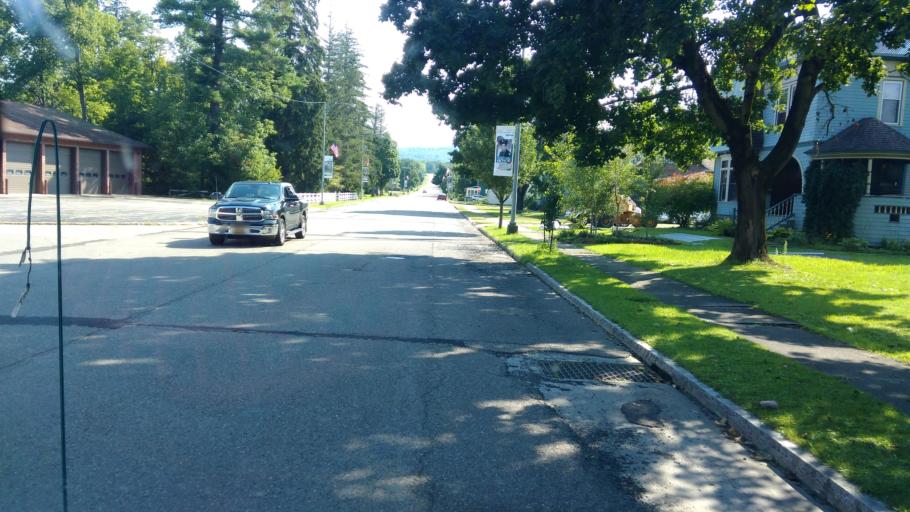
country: US
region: New York
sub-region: Allegany County
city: Cuba
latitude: 42.2179
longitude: -78.2734
